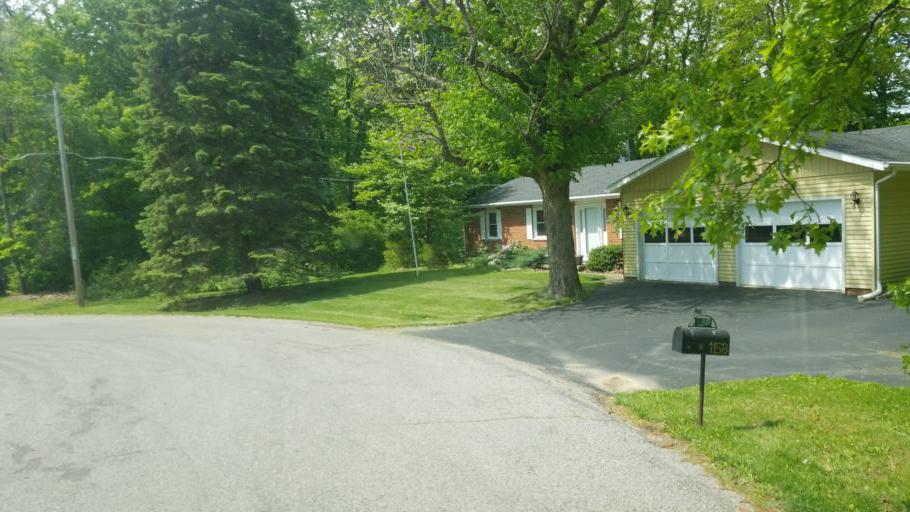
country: US
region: Ohio
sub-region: Crawford County
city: Crestline
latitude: 40.7286
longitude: -82.6916
